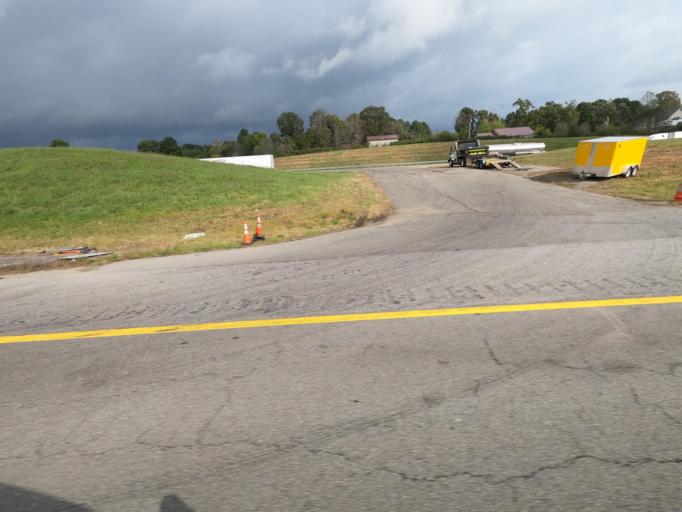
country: US
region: Tennessee
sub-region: Dickson County
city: Burns
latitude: 36.0206
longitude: -87.2622
